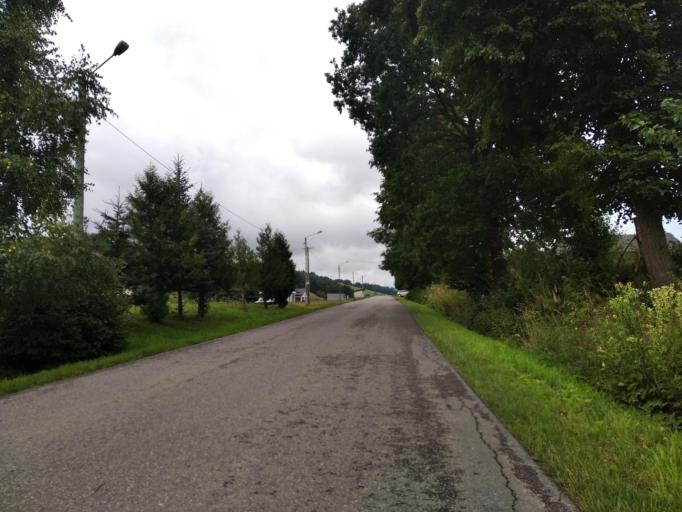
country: PL
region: Subcarpathian Voivodeship
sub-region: Powiat brzozowski
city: Nozdrzec
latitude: 49.7331
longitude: 22.2680
